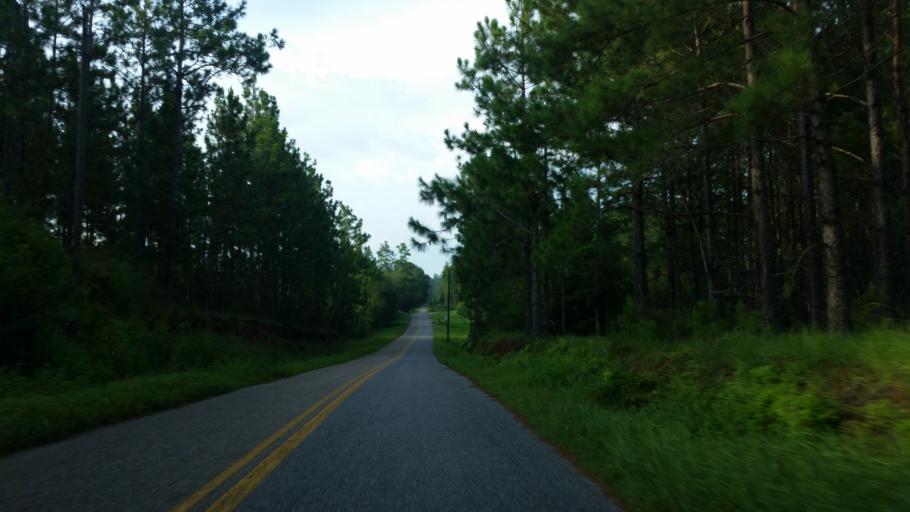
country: US
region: Alabama
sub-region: Escambia County
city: Atmore
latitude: 30.9769
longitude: -87.5712
